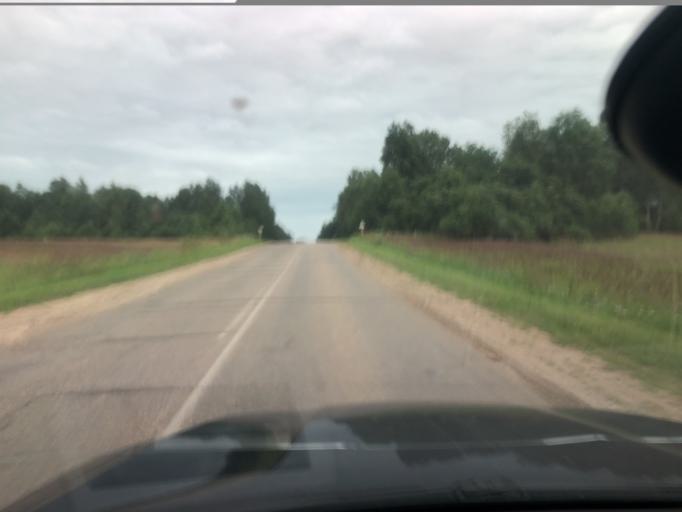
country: RU
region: Jaroslavl
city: Petrovsk
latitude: 56.9856
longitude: 39.1512
